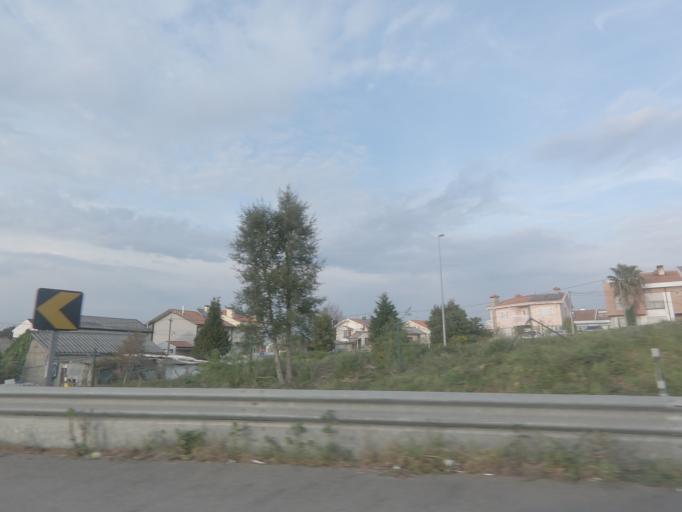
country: PT
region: Porto
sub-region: Matosinhos
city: Sao Mamede de Infesta
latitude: 41.2011
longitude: -8.6063
